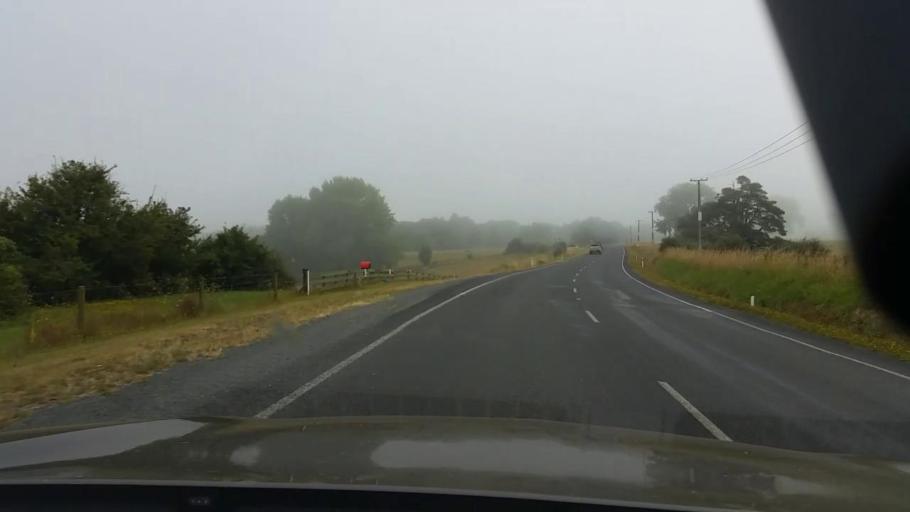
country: NZ
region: Waikato
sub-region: Hamilton City
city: Hamilton
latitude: -37.6452
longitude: 175.2958
